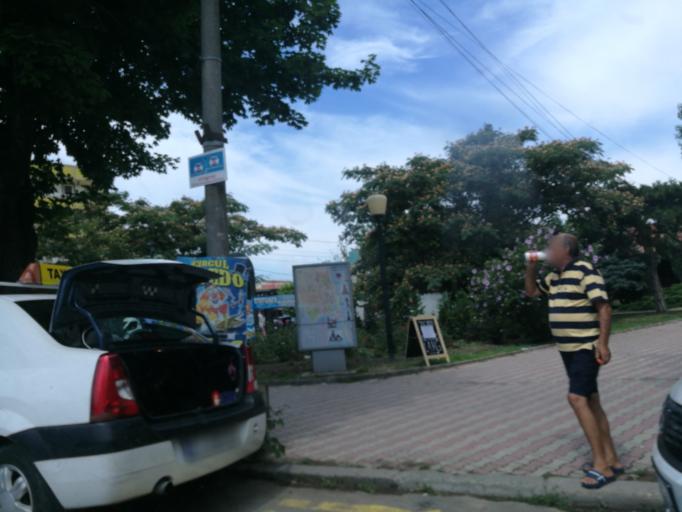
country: RO
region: Constanta
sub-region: Oras Eforie
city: Eforie Nord
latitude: 44.0644
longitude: 28.6349
